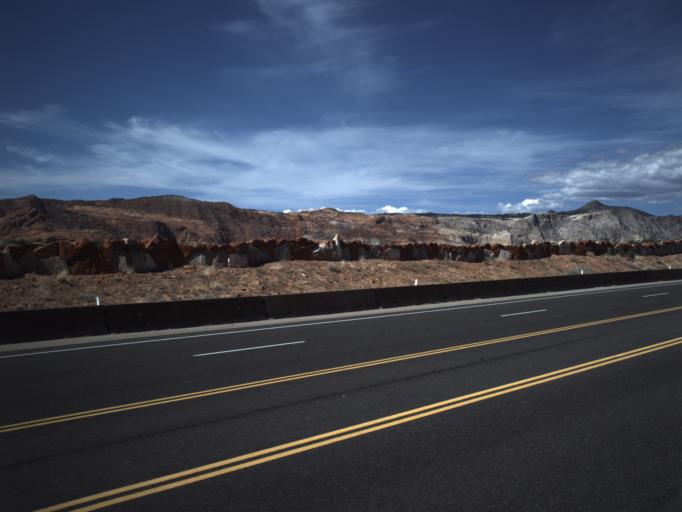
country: US
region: Utah
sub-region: Washington County
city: Ivins
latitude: 37.1989
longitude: -113.6245
